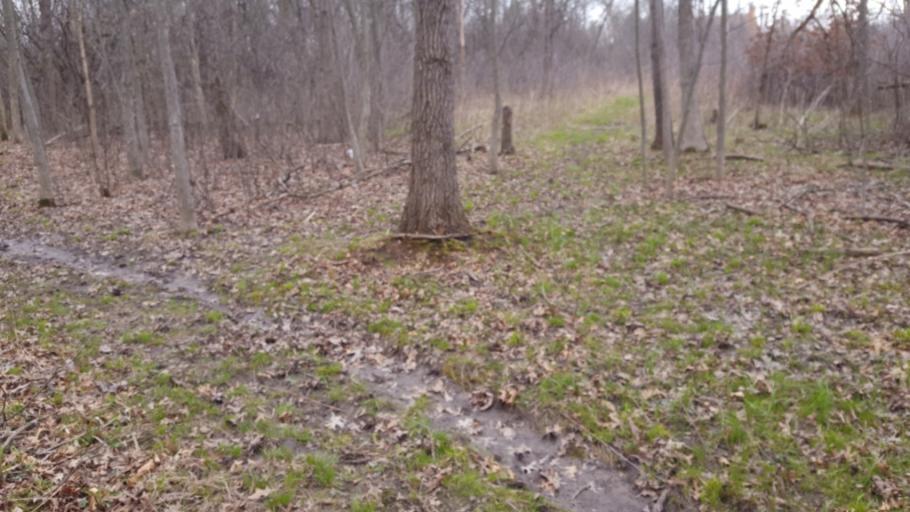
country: US
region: Illinois
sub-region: Cook County
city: Northbrook
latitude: 42.1353
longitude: -87.8183
